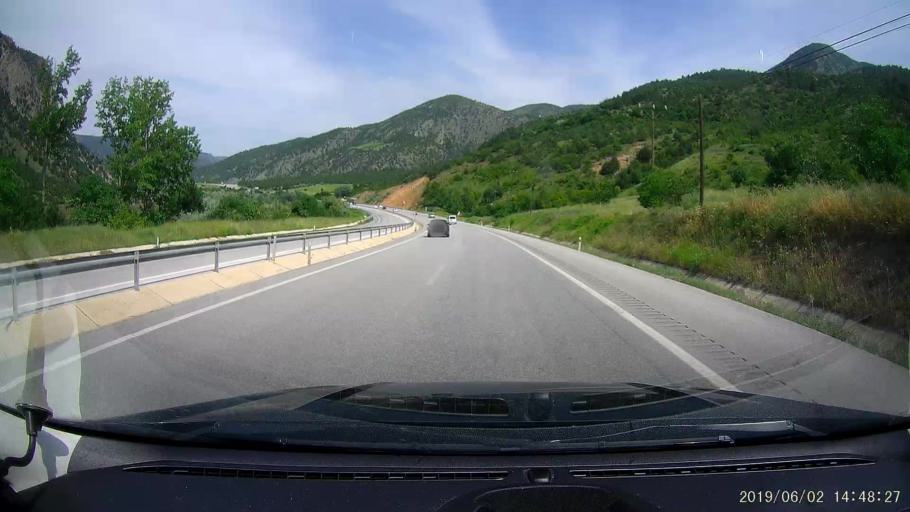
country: TR
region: Corum
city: Hacihamza
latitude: 41.0626
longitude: 34.4808
